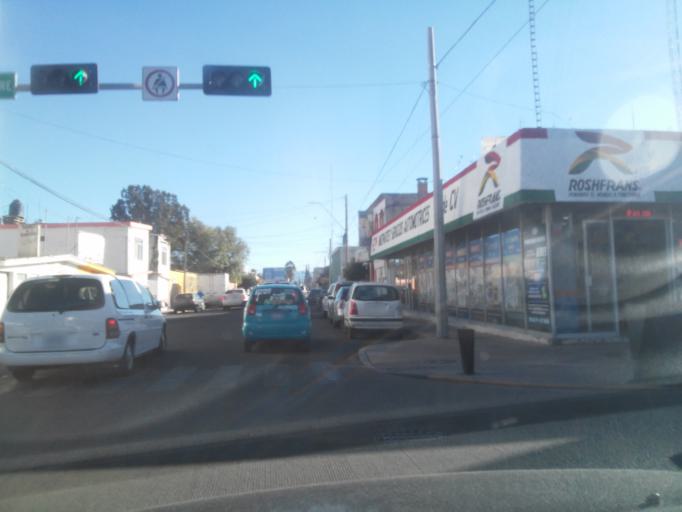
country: MX
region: Durango
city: Victoria de Durango
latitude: 24.0287
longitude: -104.6472
